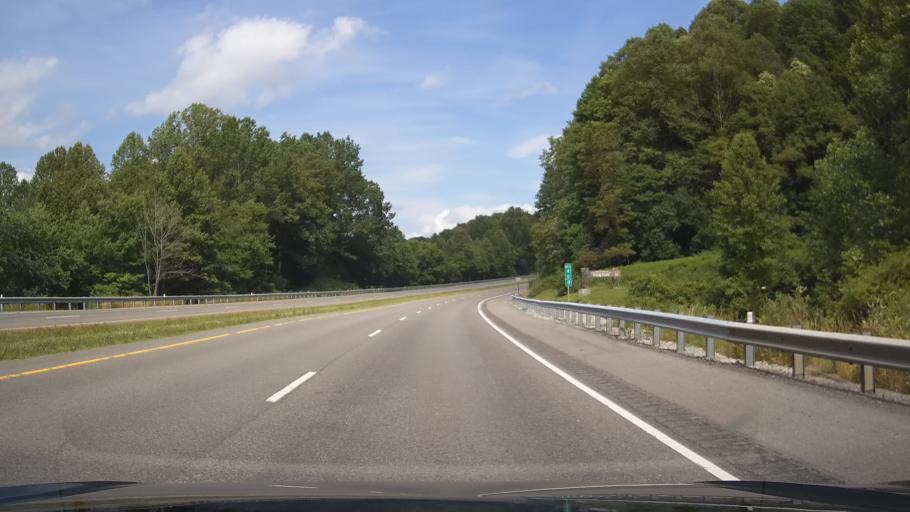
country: US
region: Virginia
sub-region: City of Norton
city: Norton
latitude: 36.9260
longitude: -82.6551
